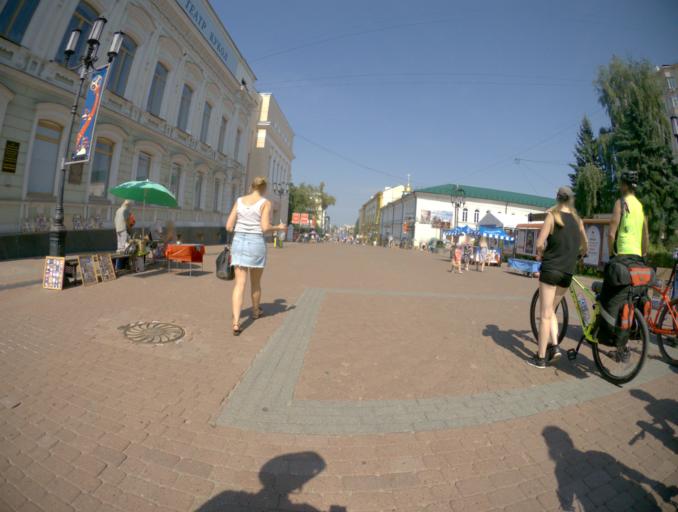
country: RU
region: Nizjnij Novgorod
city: Nizhniy Novgorod
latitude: 56.3184
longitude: 43.9962
